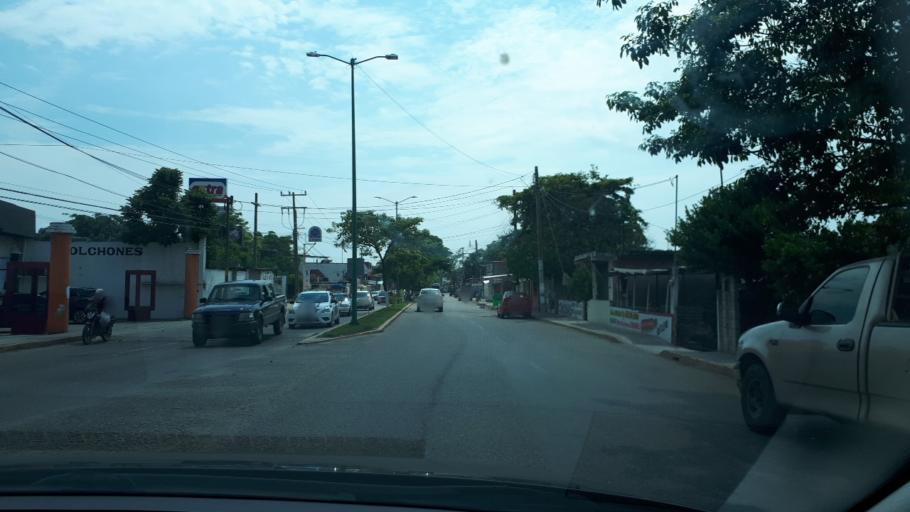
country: MX
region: Tabasco
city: Comalcalco
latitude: 18.2733
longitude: -93.2189
